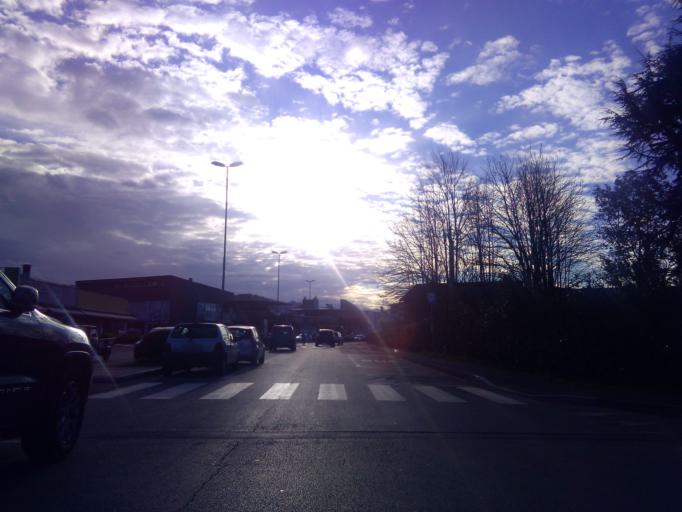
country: IT
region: Tuscany
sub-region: Provincia di Massa-Carrara
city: Carrara
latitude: 44.0525
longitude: 10.0503
